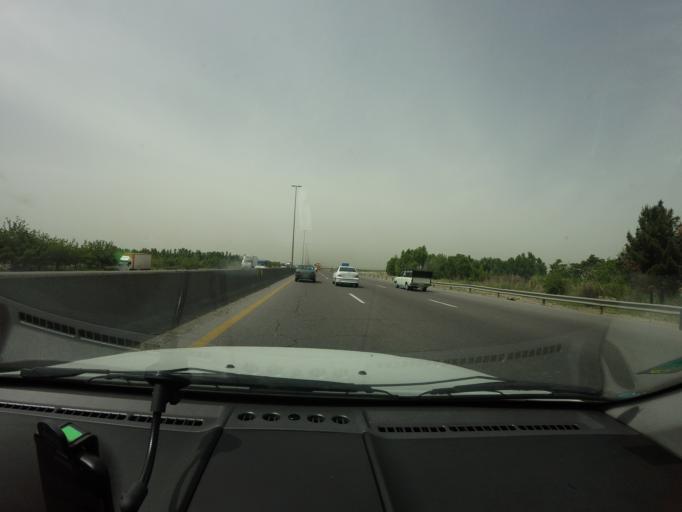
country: IR
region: Tehran
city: Eslamshahr
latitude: 35.6073
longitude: 51.1993
